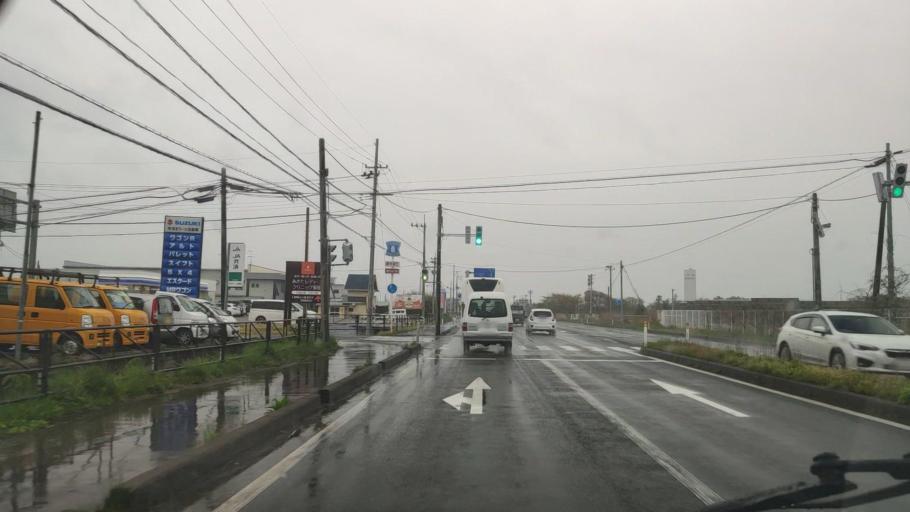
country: JP
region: Akita
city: Tenno
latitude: 39.8636
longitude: 140.0063
